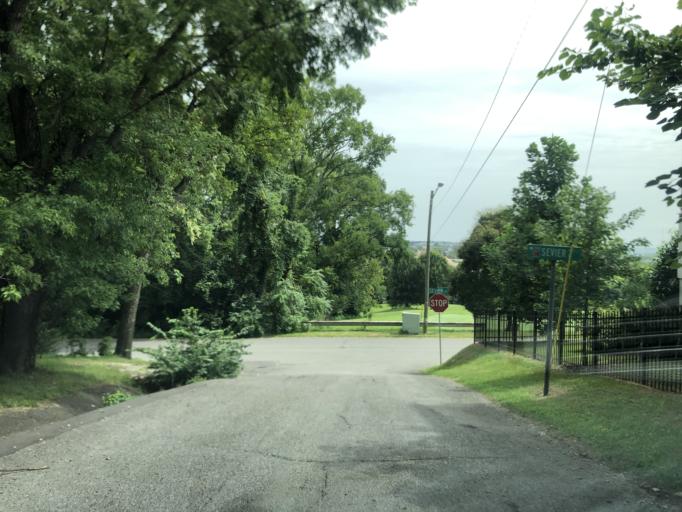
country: US
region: Tennessee
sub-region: Davidson County
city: Nashville
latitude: 36.1664
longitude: -86.7383
